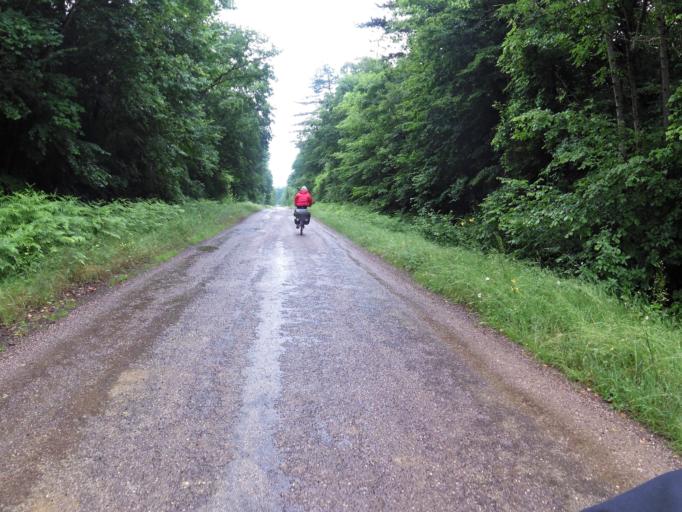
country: FR
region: Champagne-Ardenne
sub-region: Departement de la Marne
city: Sermaize-les-Bains
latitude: 48.7634
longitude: 4.9458
